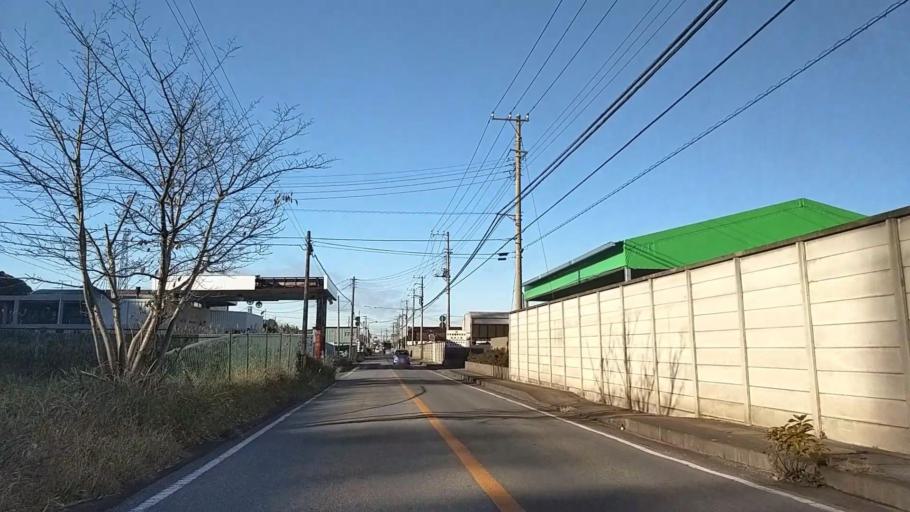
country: JP
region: Chiba
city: Kimitsu
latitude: 35.3421
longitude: 139.8717
